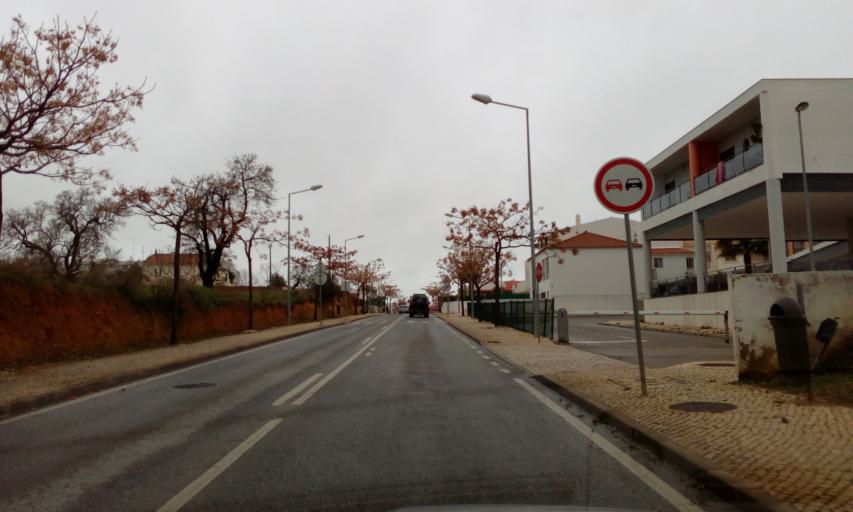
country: PT
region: Faro
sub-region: Albufeira
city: Ferreiras
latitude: 37.1277
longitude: -8.2478
